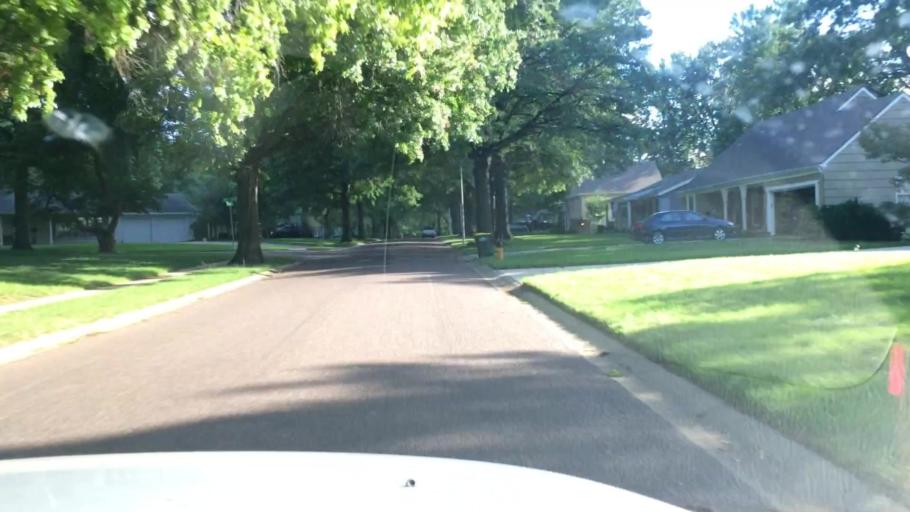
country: US
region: Kansas
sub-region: Johnson County
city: Overland Park
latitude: 38.9693
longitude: -94.6573
